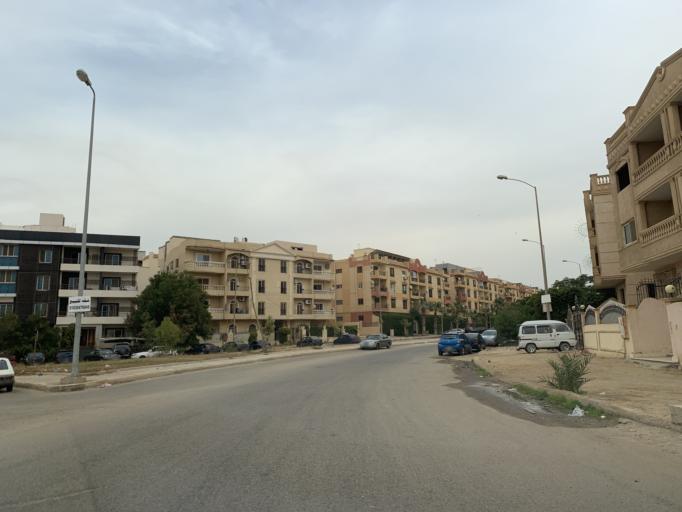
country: EG
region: Al Jizah
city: Awsim
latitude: 30.0308
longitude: 30.9805
